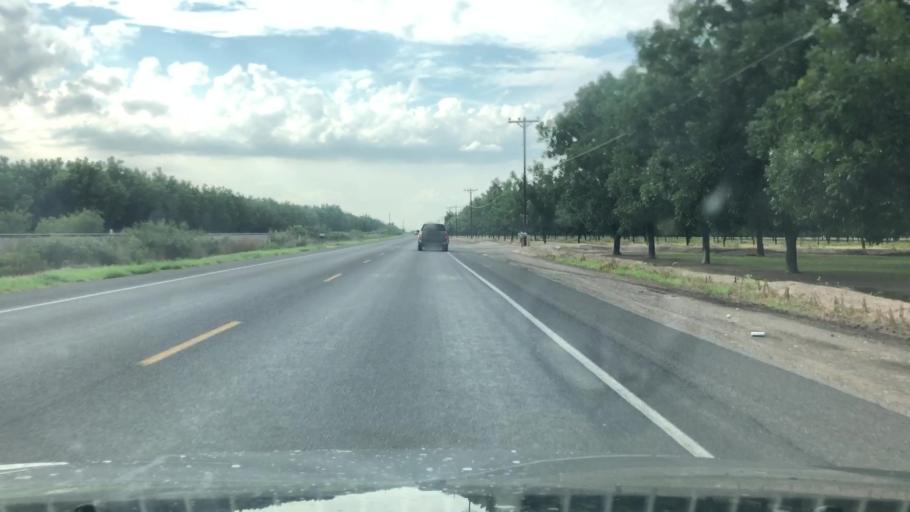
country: US
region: New Mexico
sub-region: Dona Ana County
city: Mesquite
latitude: 32.2136
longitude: -106.7274
